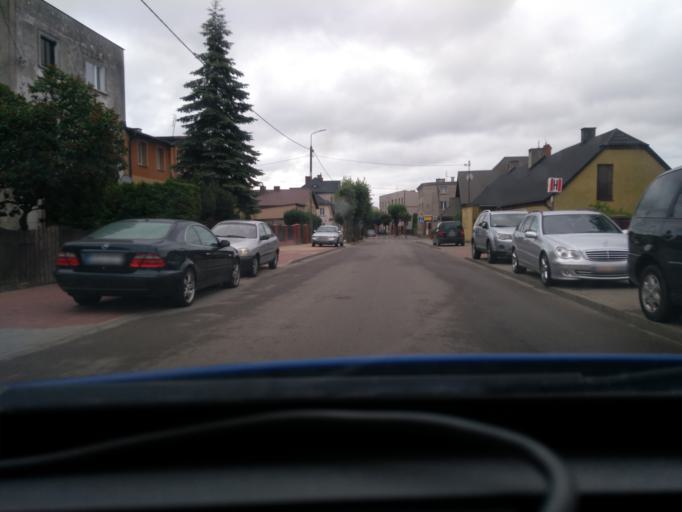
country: PL
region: Pomeranian Voivodeship
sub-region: Powiat kartuski
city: Kartuzy
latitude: 54.3391
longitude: 18.2001
